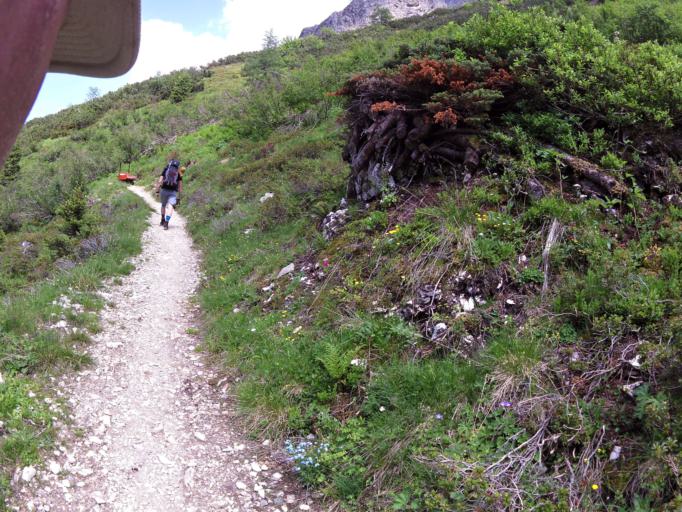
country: AT
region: Tyrol
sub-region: Politischer Bezirk Innsbruck Land
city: Gschnitz
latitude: 47.0582
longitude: 11.3164
